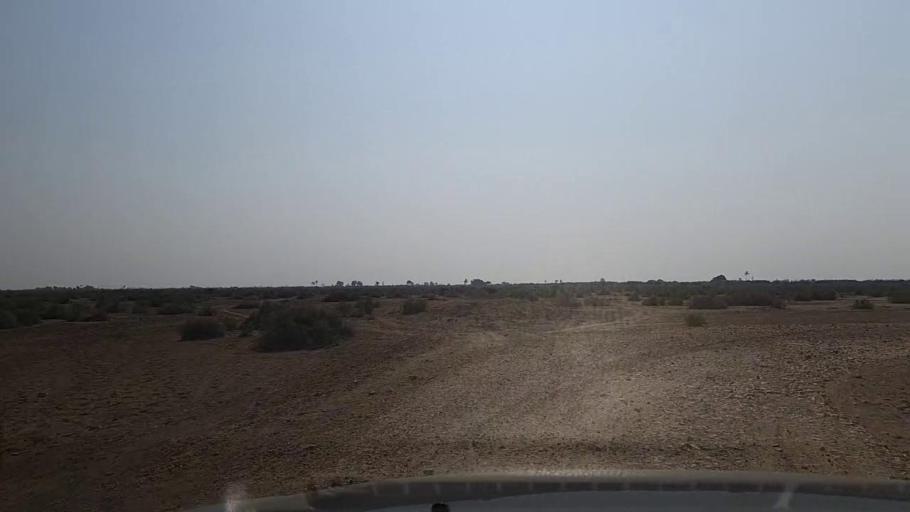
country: PK
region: Sindh
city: Mirpur Sakro
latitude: 24.4268
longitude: 67.7183
